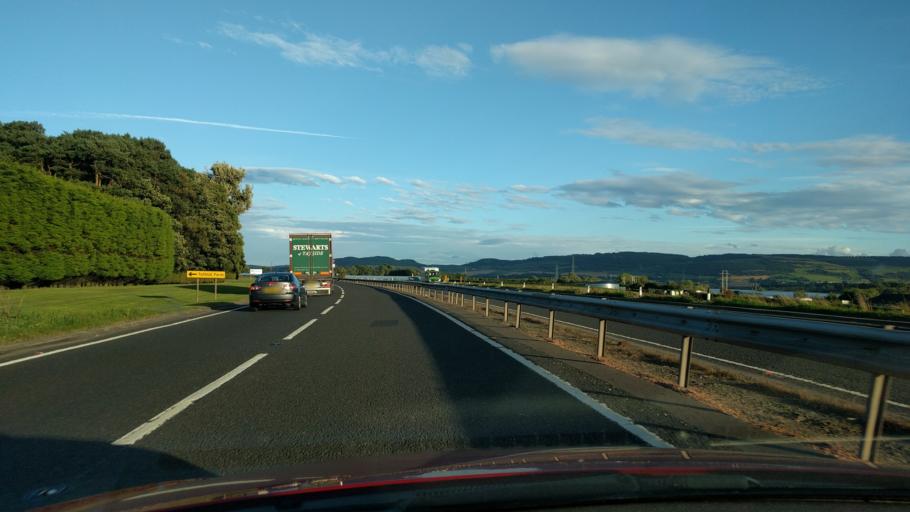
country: GB
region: Scotland
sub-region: Perth and Kinross
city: Abernethy
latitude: 56.3751
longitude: -3.3356
